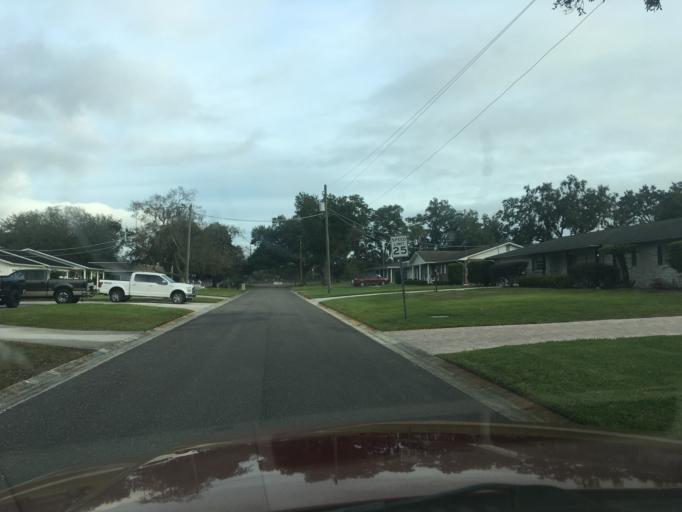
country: US
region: Florida
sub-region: Hillsborough County
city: Plant City
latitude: 28.0347
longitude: -82.0996
